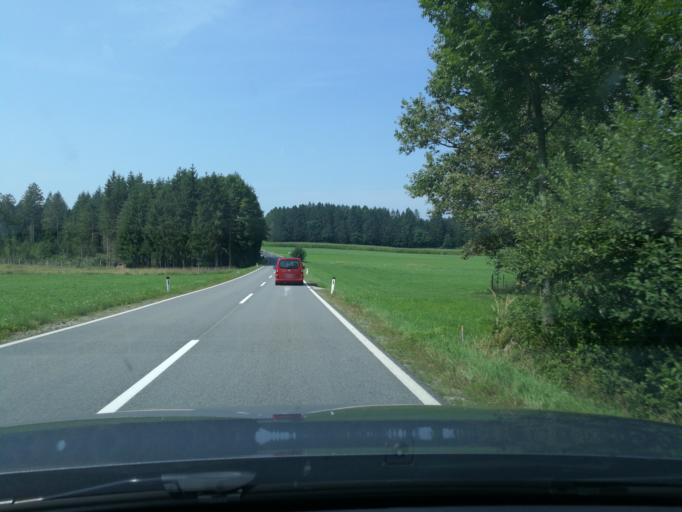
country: AT
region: Upper Austria
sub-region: Politischer Bezirk Grieskirchen
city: Grieskirchen
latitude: 48.3521
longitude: 13.7174
